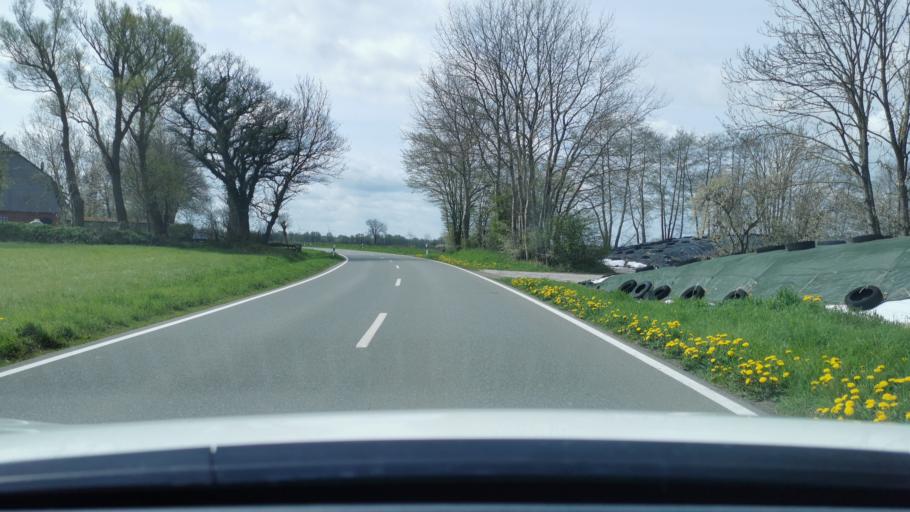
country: DE
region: Schleswig-Holstein
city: Oldenbuttel
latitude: 54.1916
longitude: 9.4532
